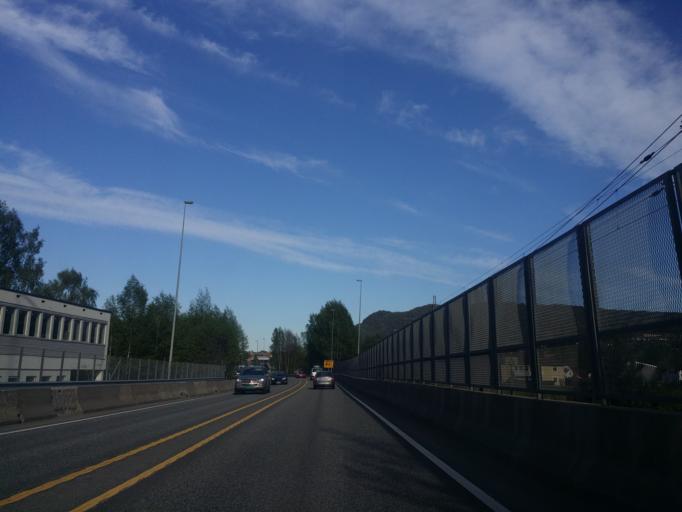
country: NO
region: Buskerud
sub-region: Nedre Eiker
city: Mjondalen
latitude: 59.7530
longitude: 9.9972
